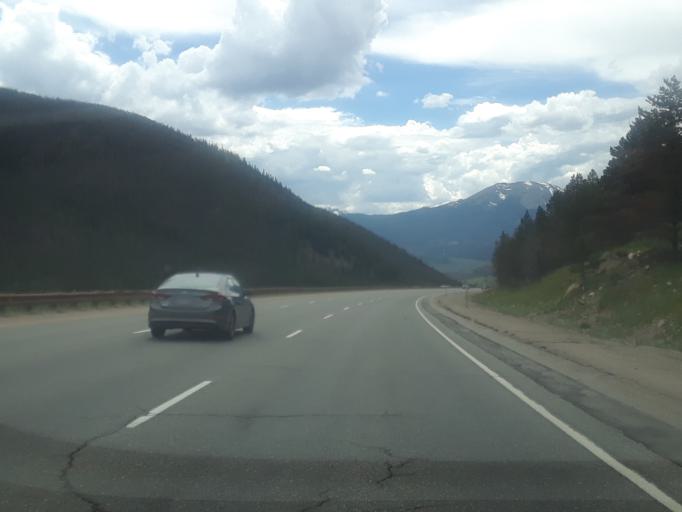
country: US
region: Colorado
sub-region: Summit County
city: Keystone
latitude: 39.6551
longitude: -105.9988
